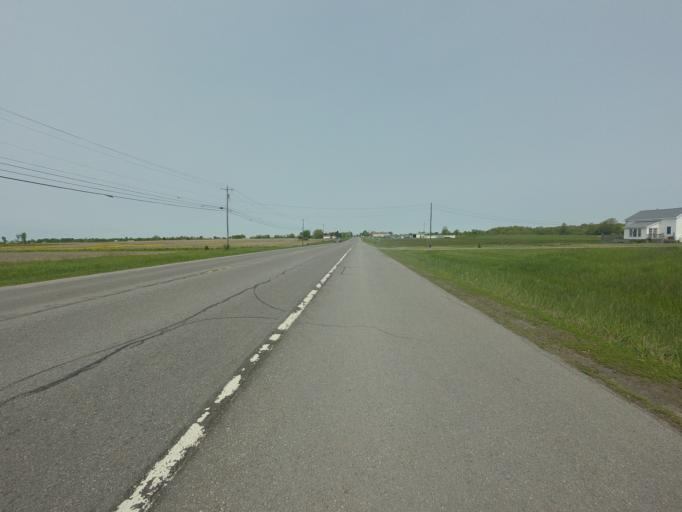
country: US
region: New York
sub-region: Jefferson County
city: Dexter
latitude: 44.0560
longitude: -76.1098
